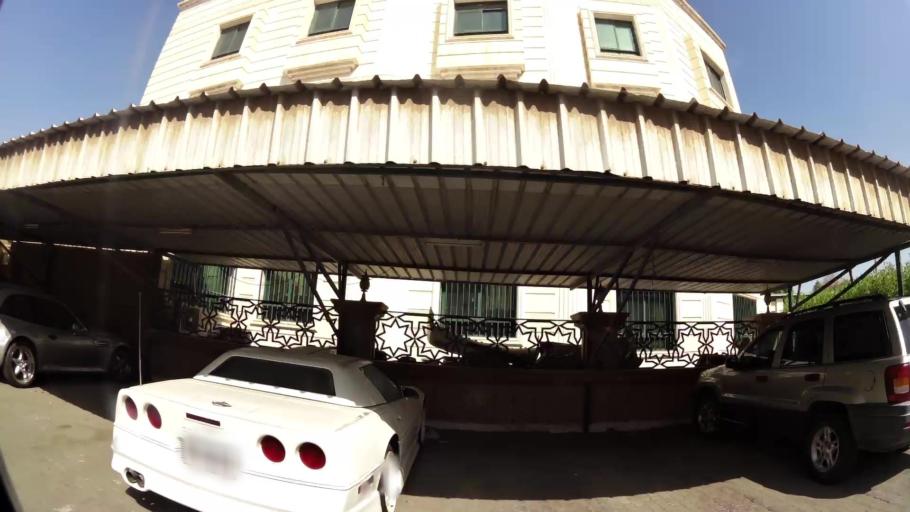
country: KW
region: Muhafazat Hawalli
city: Salwa
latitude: 29.2819
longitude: 48.0786
